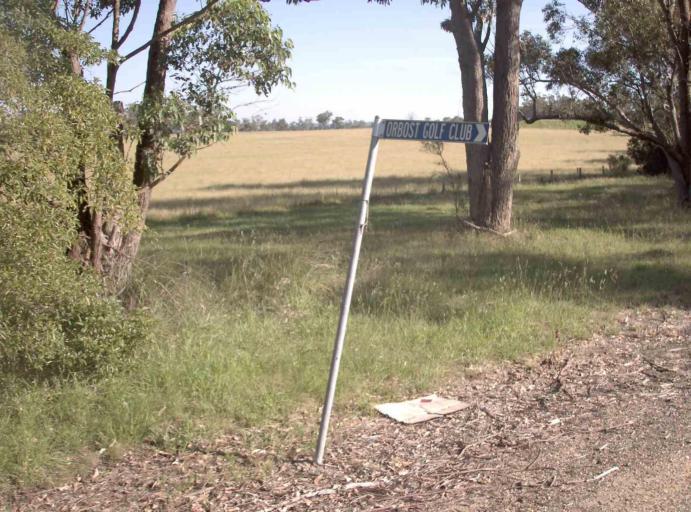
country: AU
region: Victoria
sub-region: East Gippsland
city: Lakes Entrance
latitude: -37.6951
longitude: 148.4666
